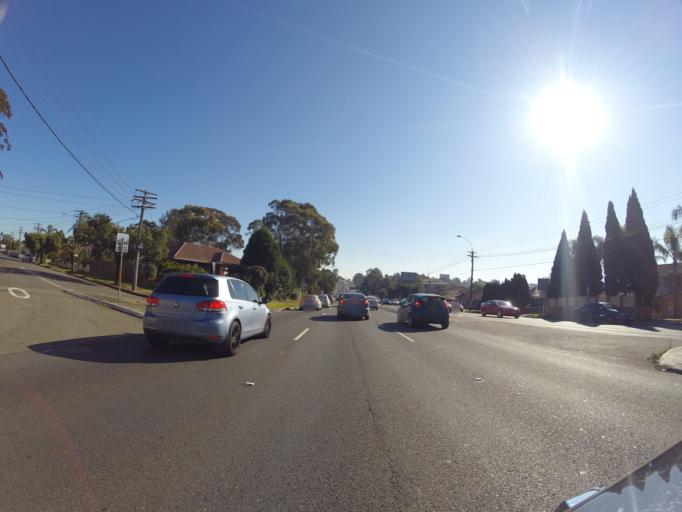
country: AU
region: New South Wales
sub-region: Canterbury
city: Roselands
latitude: -33.9393
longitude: 151.0753
